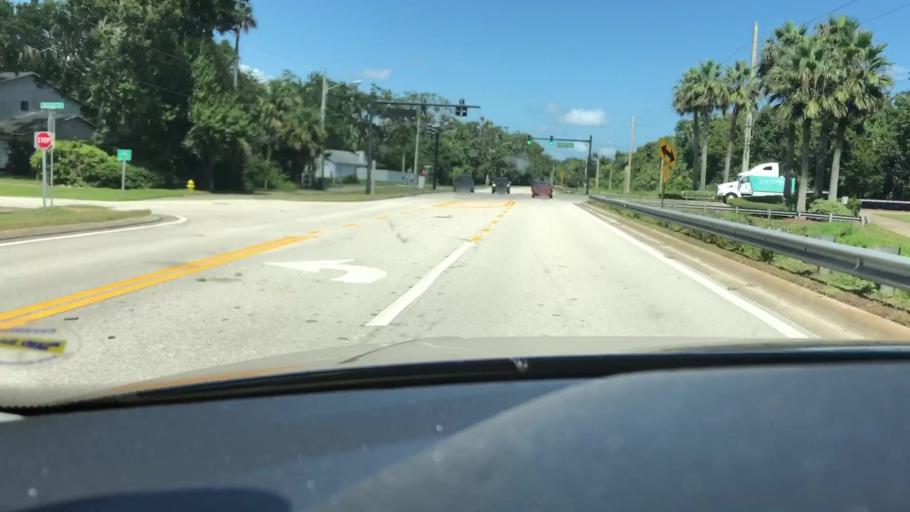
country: US
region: Florida
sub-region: Volusia County
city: Port Orange
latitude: 29.1306
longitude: -80.9933
